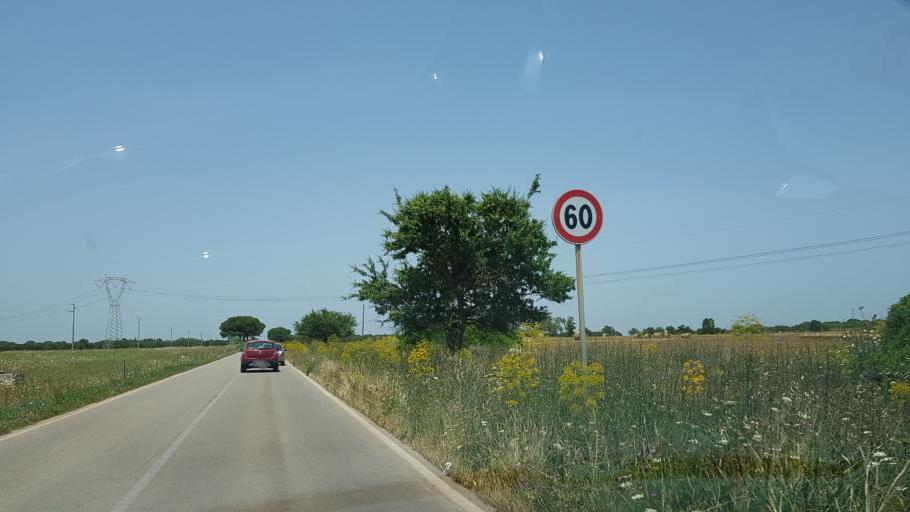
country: IT
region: Apulia
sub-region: Provincia di Brindisi
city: San Pancrazio Salentino
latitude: 40.3405
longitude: 17.8489
